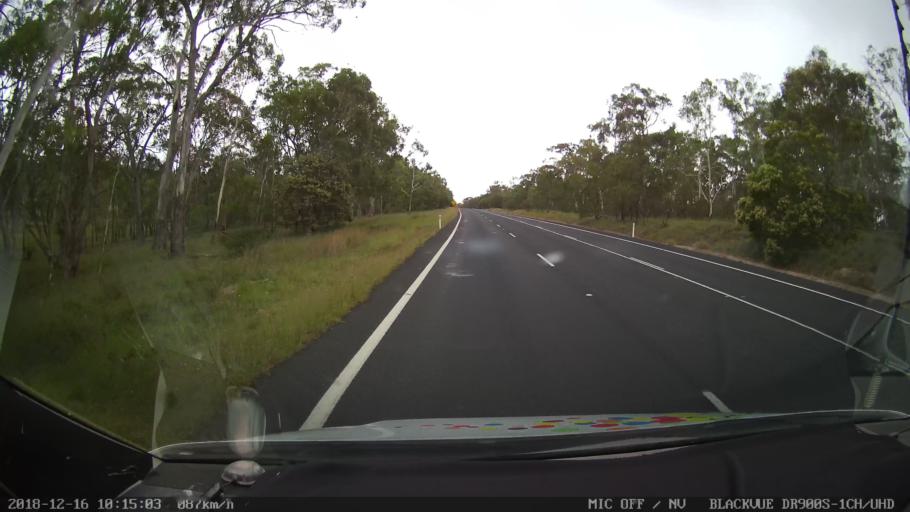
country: AU
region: New South Wales
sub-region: Tenterfield Municipality
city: Carrolls Creek
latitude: -29.2808
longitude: 151.9690
